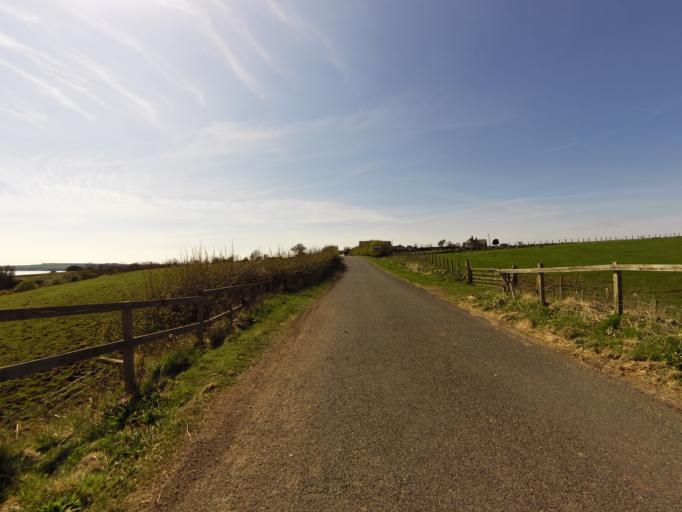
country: GB
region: Scotland
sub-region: Angus
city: Montrose
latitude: 56.6666
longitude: -2.5058
